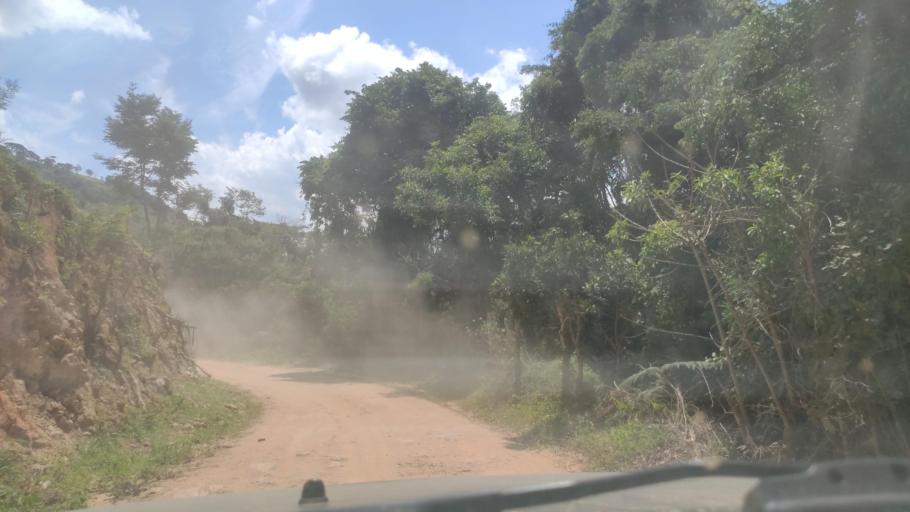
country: BR
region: Minas Gerais
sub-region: Cambui
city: Cambui
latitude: -22.6948
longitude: -45.9869
